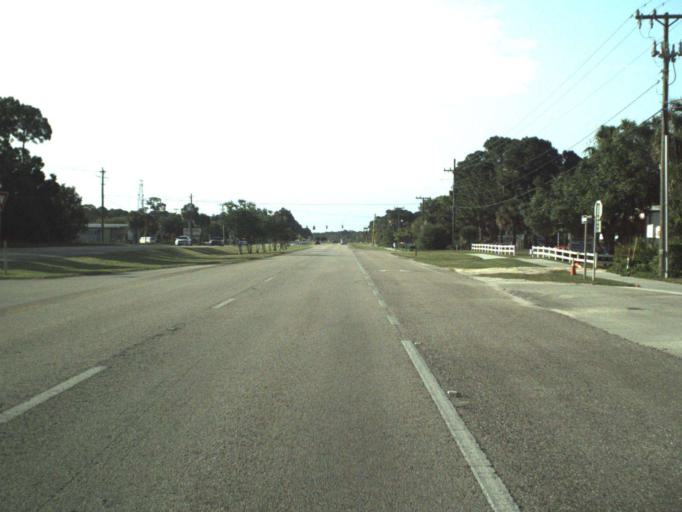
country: US
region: Florida
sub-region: Volusia County
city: Edgewater
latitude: 28.9449
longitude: -80.8828
